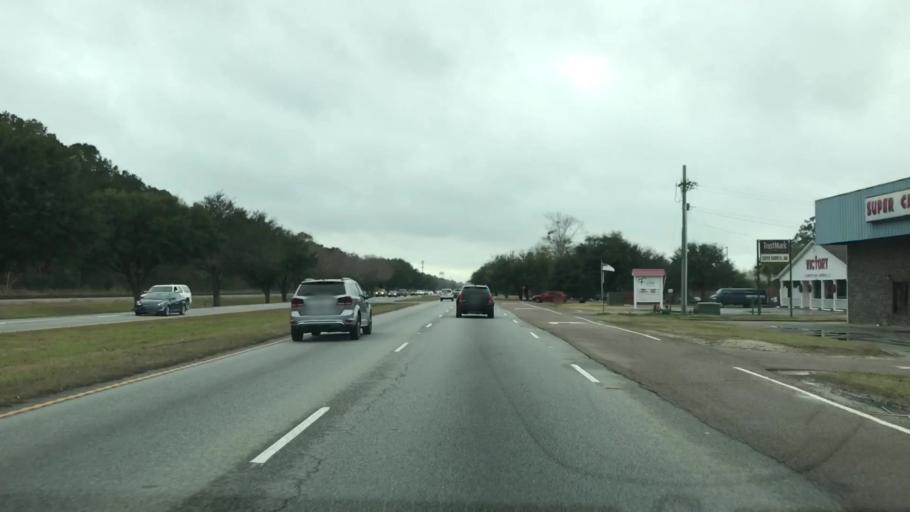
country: US
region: South Carolina
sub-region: Berkeley County
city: Goose Creek
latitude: 33.0304
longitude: -80.0348
